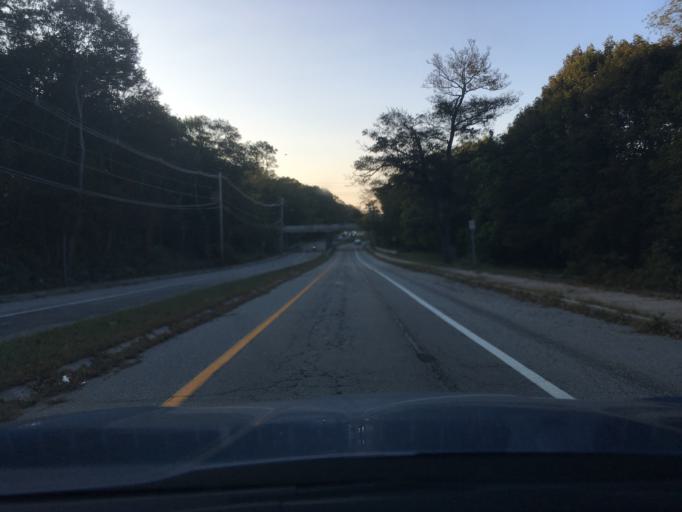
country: US
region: Rhode Island
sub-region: Kent County
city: East Greenwich
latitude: 41.6469
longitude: -71.4557
